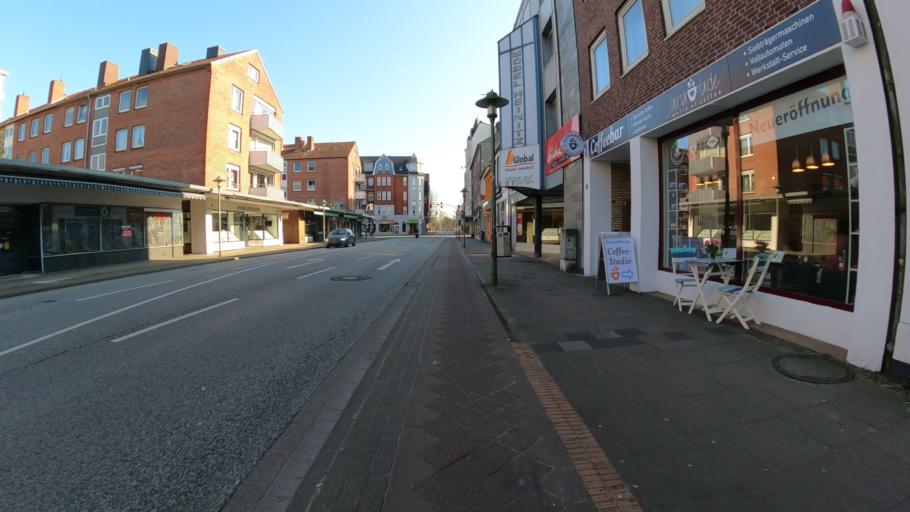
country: DE
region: Schleswig-Holstein
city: Elmshorn
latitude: 53.7550
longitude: 9.6564
